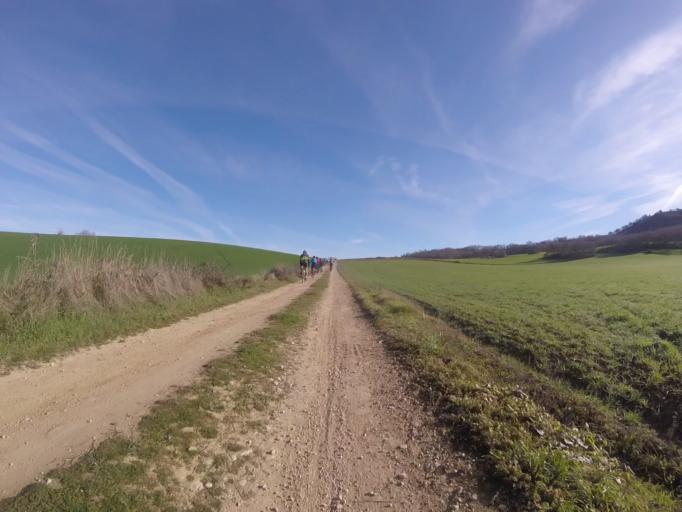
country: ES
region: Navarre
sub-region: Provincia de Navarra
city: Villatuerta
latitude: 42.6623
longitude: -1.9641
